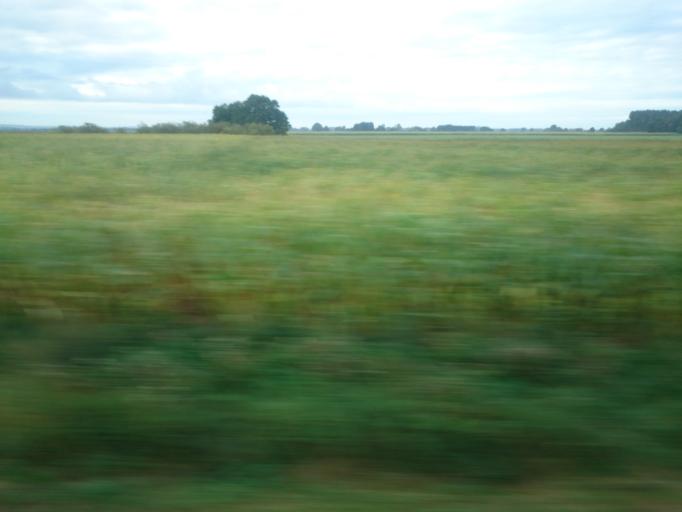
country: DE
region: Mecklenburg-Vorpommern
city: Ferdinandshof
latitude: 53.6996
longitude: 13.8650
